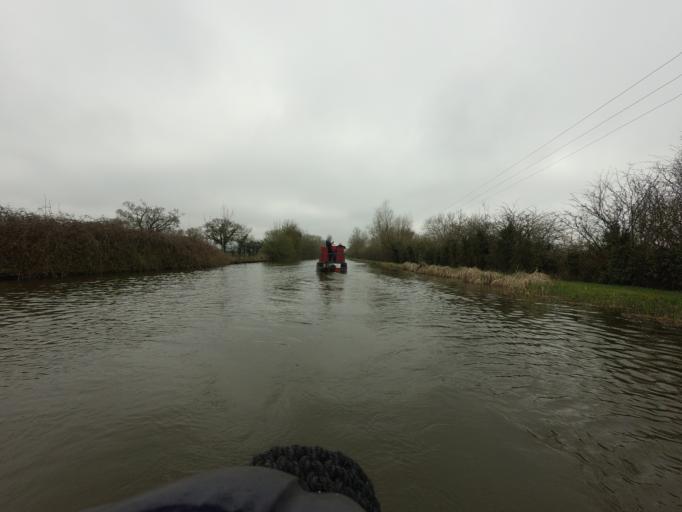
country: GB
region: England
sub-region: Buckinghamshire
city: Cheddington
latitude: 51.8601
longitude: -0.6469
